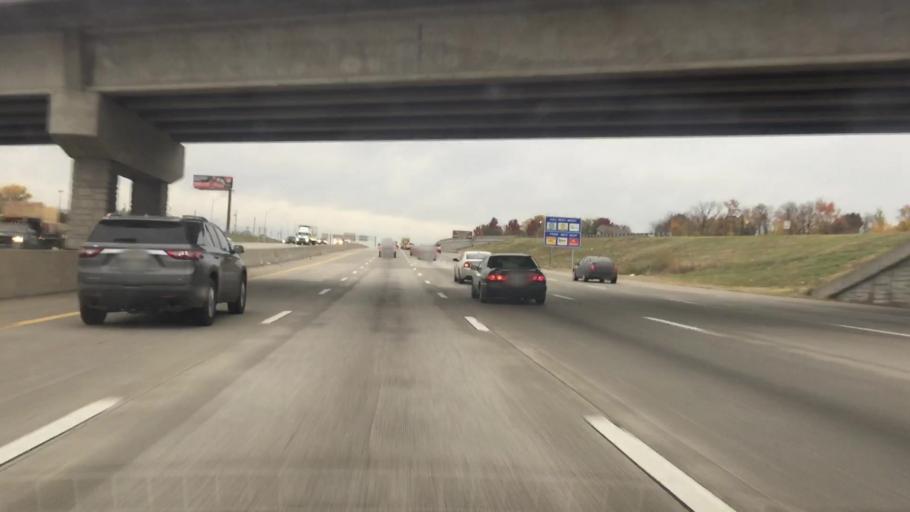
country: US
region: Missouri
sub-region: Jackson County
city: Grandview
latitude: 38.9165
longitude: -94.5270
